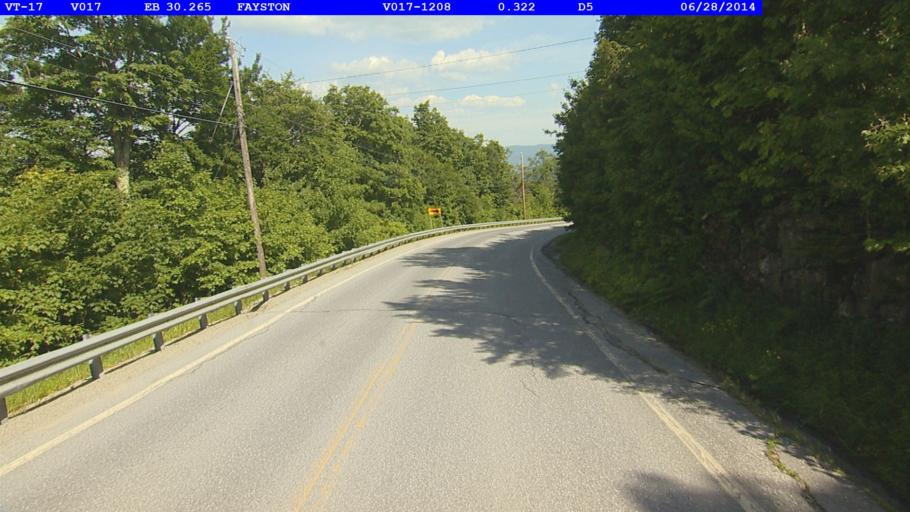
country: US
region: Vermont
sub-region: Addison County
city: Bristol
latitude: 44.2063
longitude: -72.9237
